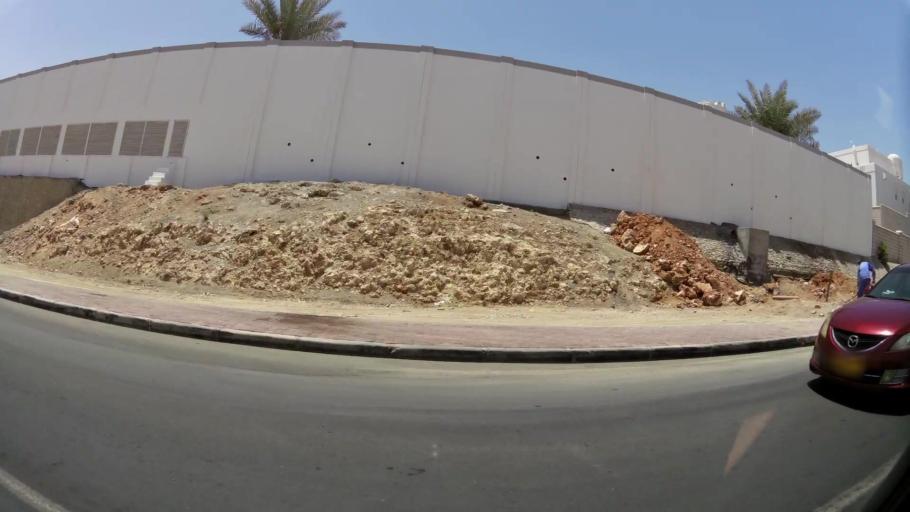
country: OM
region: Muhafazat Masqat
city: Bawshar
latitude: 23.6085
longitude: 58.4730
